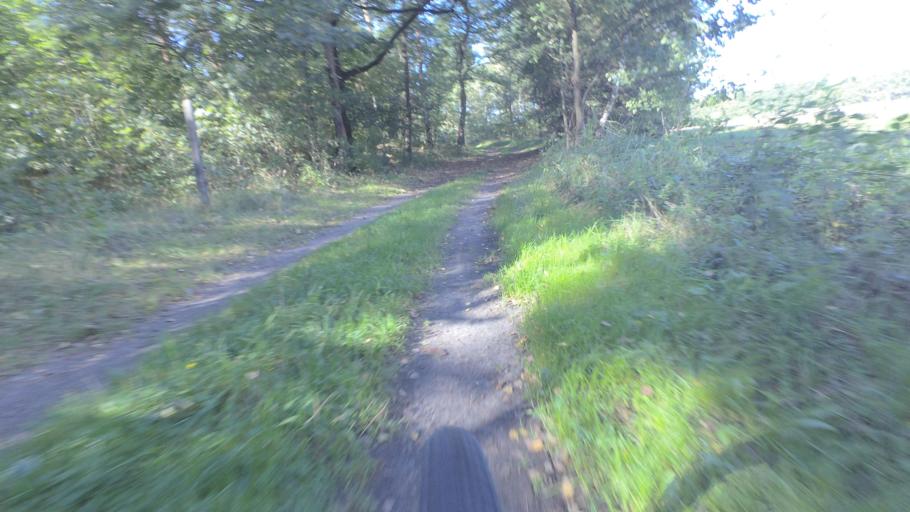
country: DE
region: Brandenburg
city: Sperenberg
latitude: 52.1431
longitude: 13.3521
